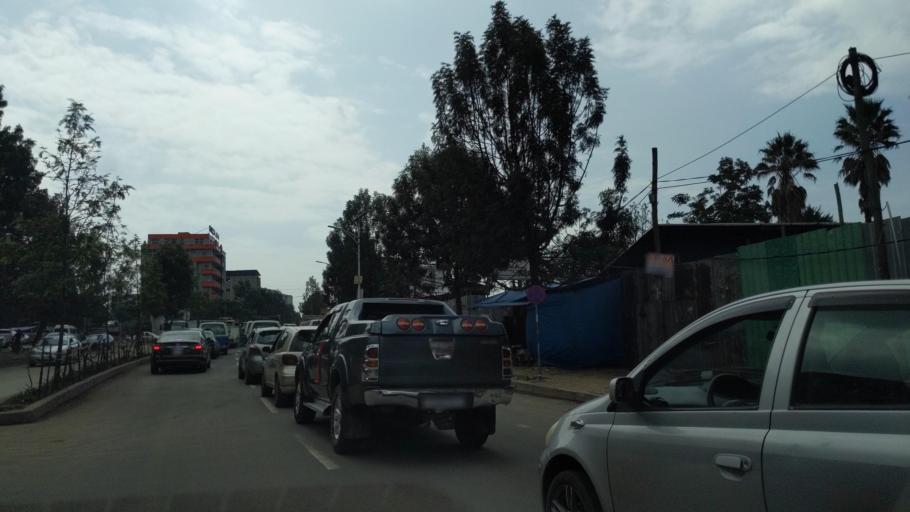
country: ET
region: Adis Abeba
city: Addis Ababa
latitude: 9.0028
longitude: 38.7993
